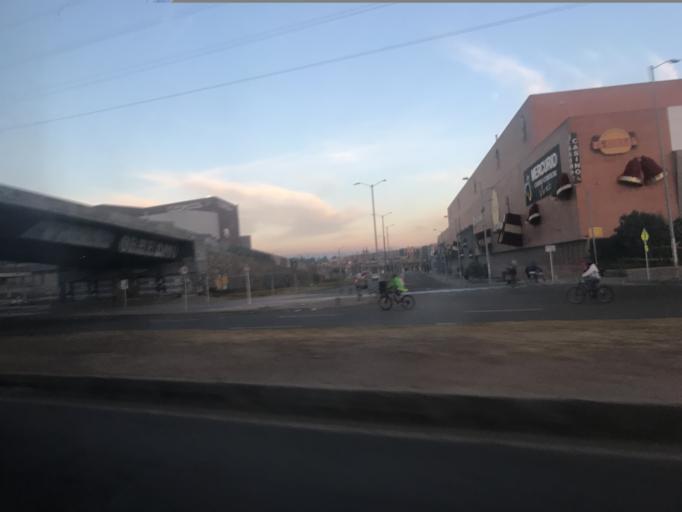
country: CO
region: Cundinamarca
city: Soacha
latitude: 4.5871
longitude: -74.2035
